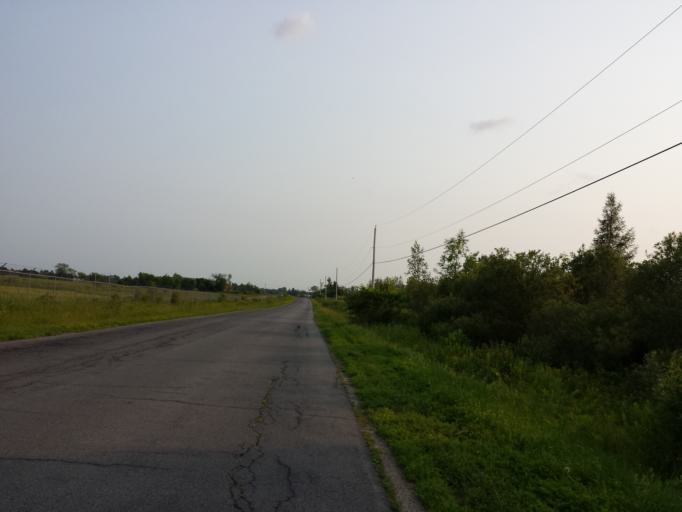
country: US
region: New York
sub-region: St. Lawrence County
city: Potsdam
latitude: 44.6748
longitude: -74.9549
